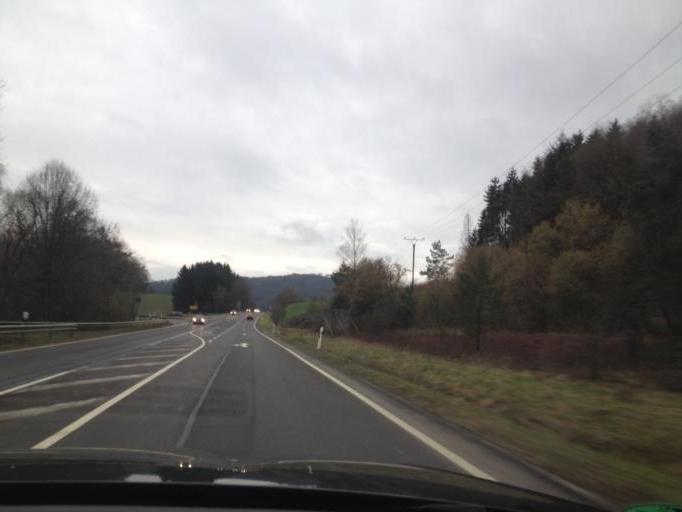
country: DE
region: Rheinland-Pfalz
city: Ellweiler
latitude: 49.6153
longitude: 7.1596
